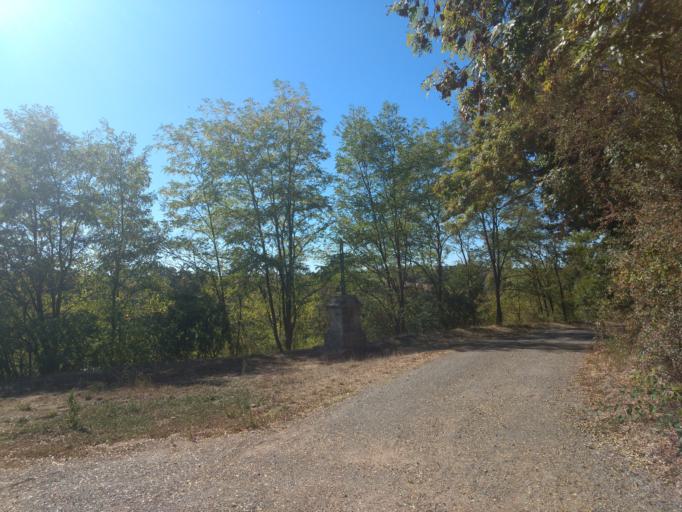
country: FR
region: Midi-Pyrenees
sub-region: Departement de l'Aveyron
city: Olemps
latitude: 44.3564
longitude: 2.5562
